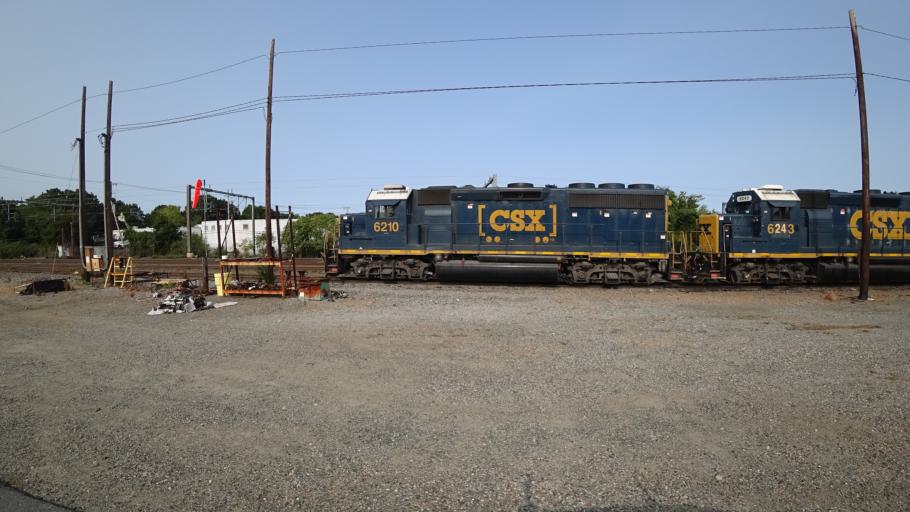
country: US
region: Massachusetts
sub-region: Norfolk County
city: Dedham
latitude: 42.2317
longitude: -71.1362
